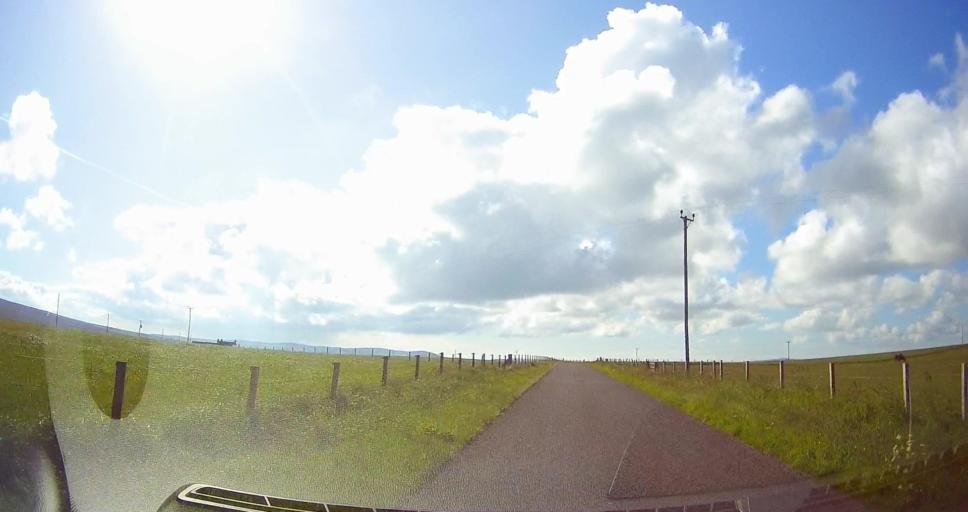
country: GB
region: Scotland
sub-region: Orkney Islands
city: Stromness
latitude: 58.9879
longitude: -3.1508
